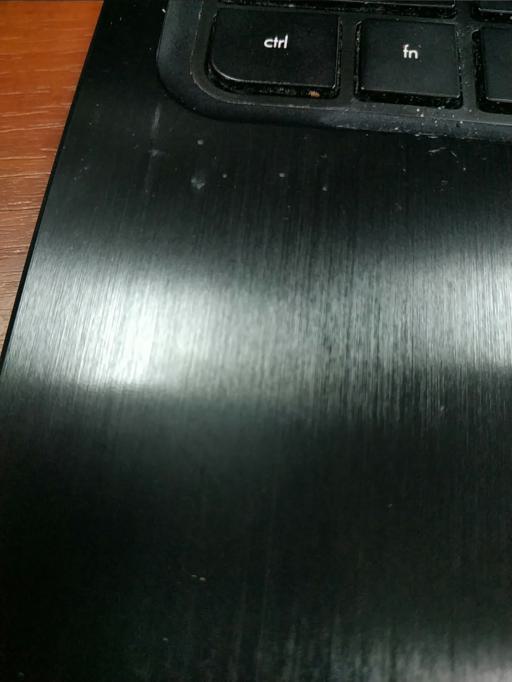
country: RU
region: Moskovskaya
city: Lyubuchany
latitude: 55.2651
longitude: 37.5933
